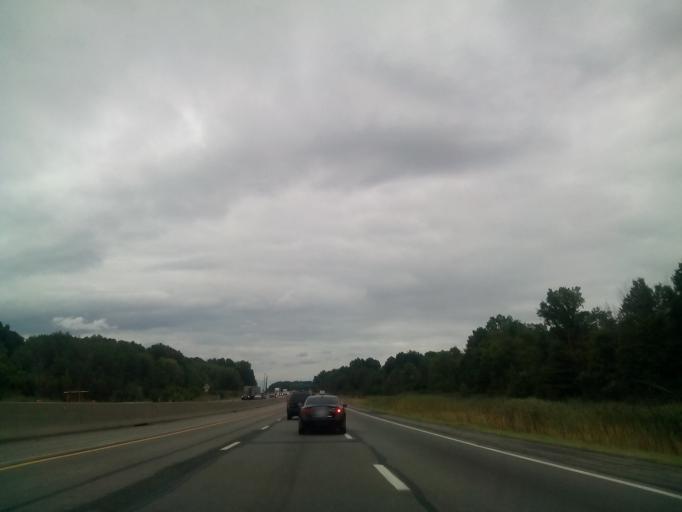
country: US
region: Ohio
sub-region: Lorain County
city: Amherst
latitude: 41.3773
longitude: -82.2370
